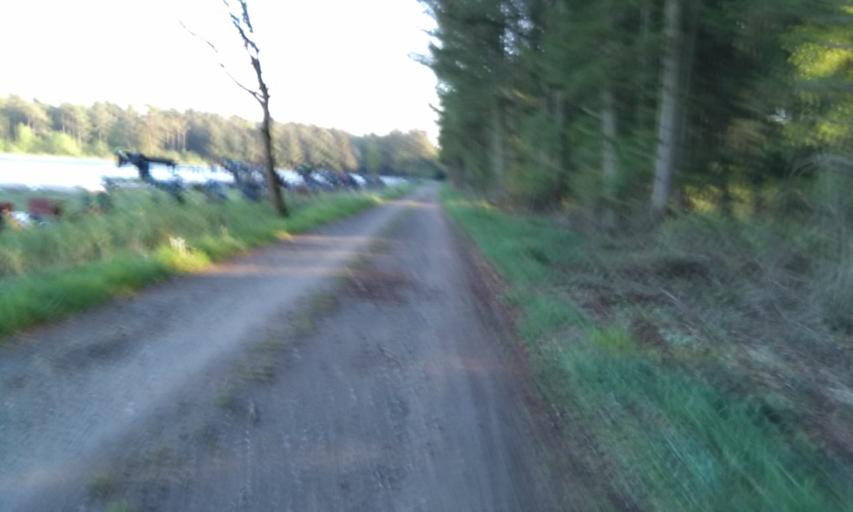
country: DE
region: Lower Saxony
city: Dollern
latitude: 53.5273
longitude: 9.5424
